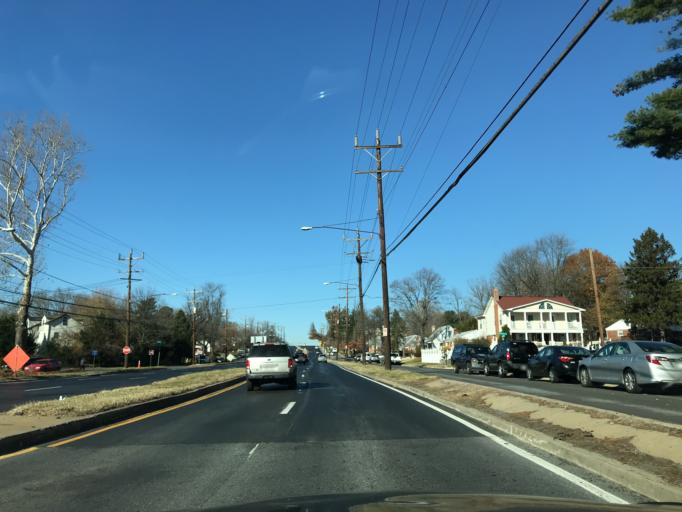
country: US
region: Maryland
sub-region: Montgomery County
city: North Kensington
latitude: 39.0533
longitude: -77.0771
